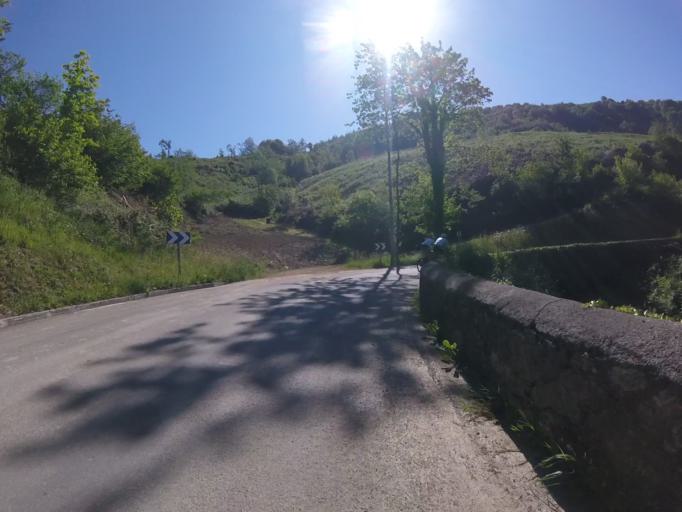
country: ES
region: Basque Country
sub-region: Provincia de Guipuzcoa
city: Beizama
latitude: 43.1295
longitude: -2.1955
